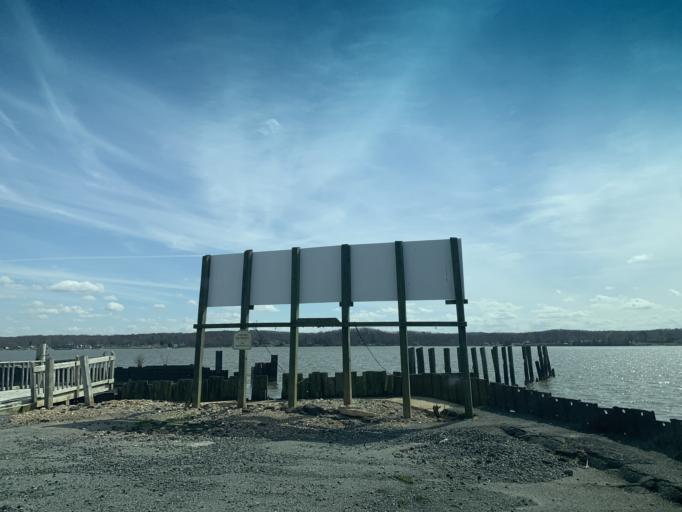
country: US
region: Maryland
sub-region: Cecil County
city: Charlestown
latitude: 39.5708
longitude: -75.9692
